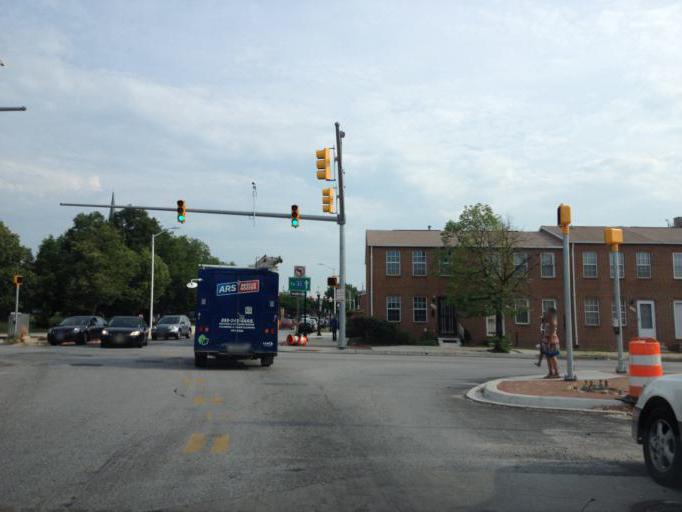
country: US
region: Maryland
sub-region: City of Baltimore
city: Baltimore
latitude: 39.2979
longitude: -76.5999
